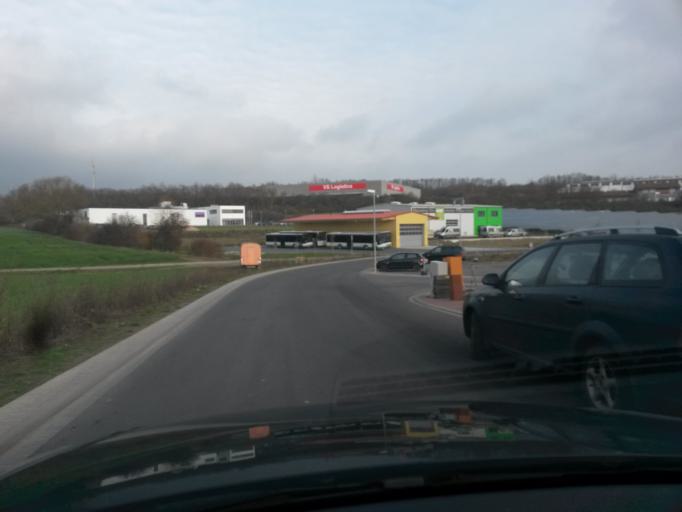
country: DE
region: Bavaria
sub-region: Regierungsbezirk Unterfranken
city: Estenfeld
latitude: 49.8413
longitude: 10.0112
